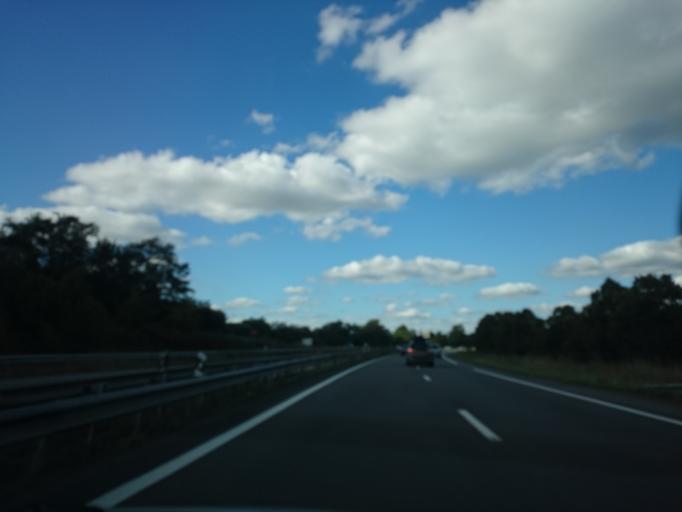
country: FR
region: Pays de la Loire
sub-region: Departement de la Loire-Atlantique
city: Heric
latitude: 47.4165
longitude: -1.6419
